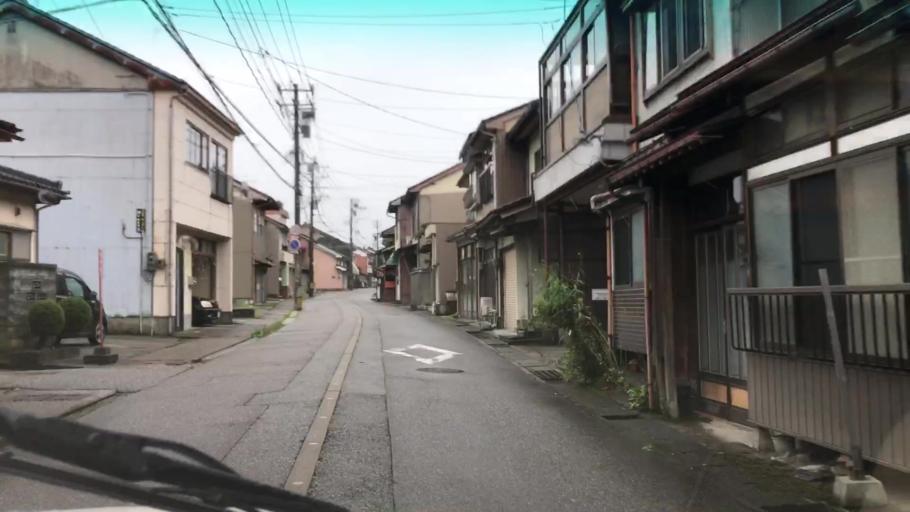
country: JP
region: Toyama
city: Kamiichi
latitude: 36.6608
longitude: 137.3179
